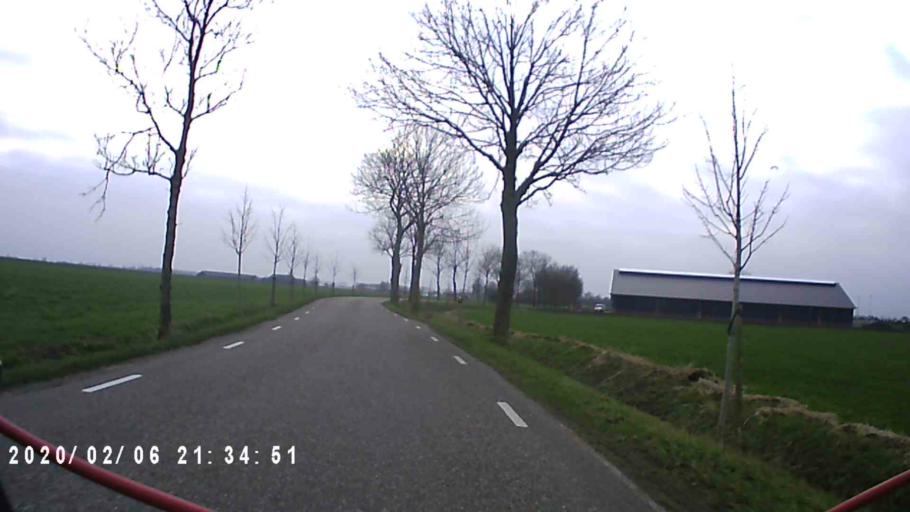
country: NL
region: Groningen
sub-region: Gemeente Zuidhorn
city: Noordhorn
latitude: 53.2721
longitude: 6.3906
